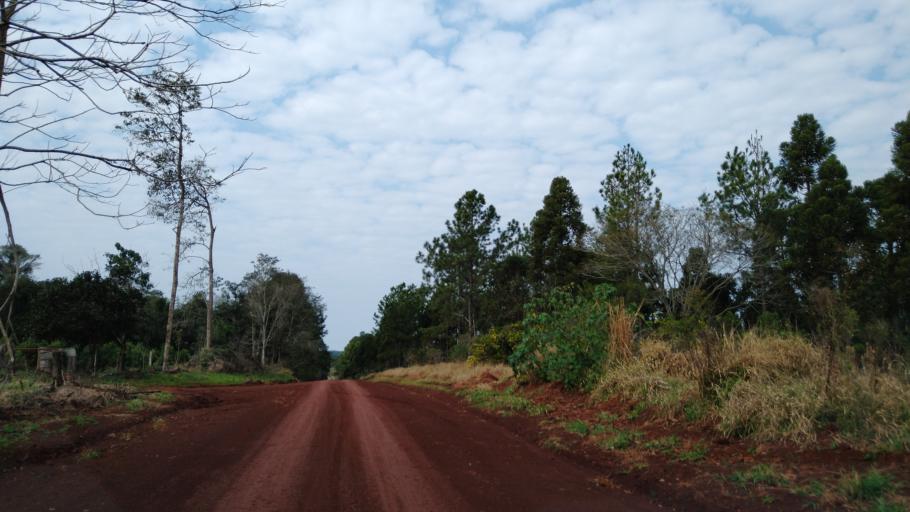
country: AR
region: Misiones
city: Ruiz de Montoya
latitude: -26.9583
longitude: -55.0600
